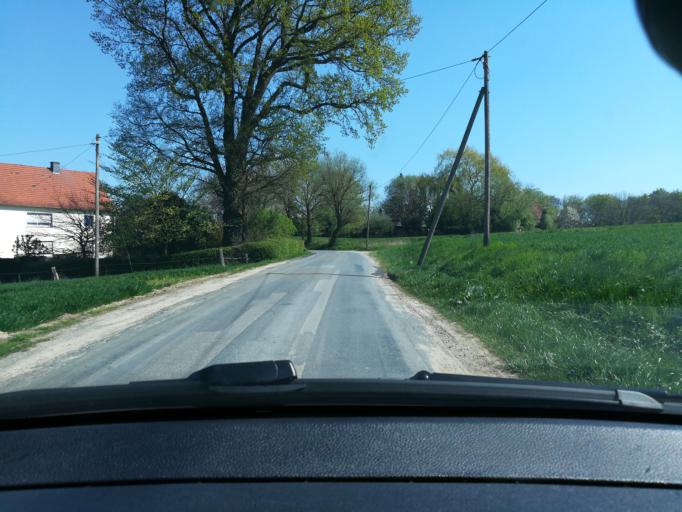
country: DE
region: North Rhine-Westphalia
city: Halle
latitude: 52.0735
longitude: 8.3806
